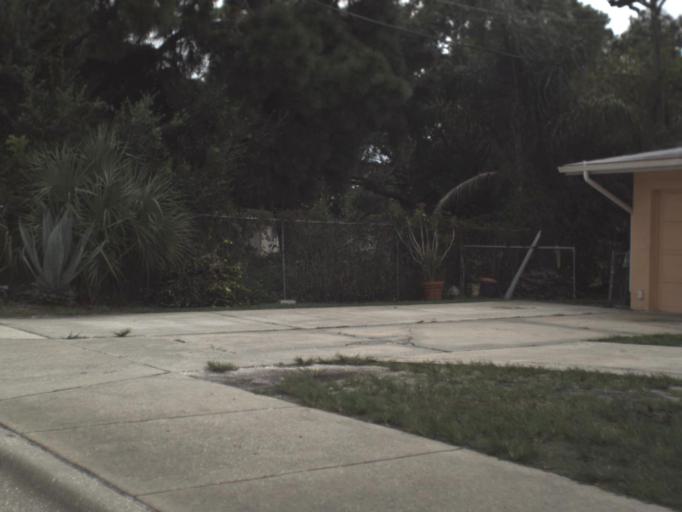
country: US
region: Florida
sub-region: Sarasota County
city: Sarasota Springs
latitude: 27.2989
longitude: -82.4698
